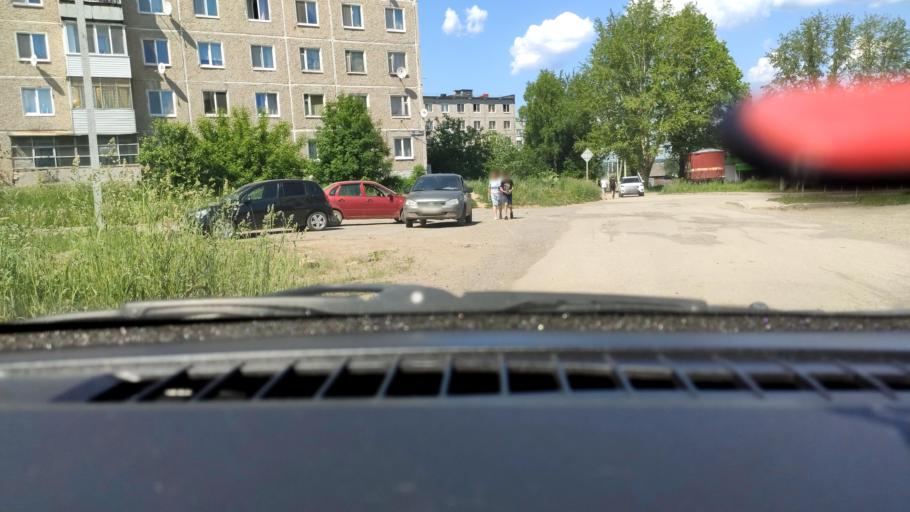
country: RU
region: Perm
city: Sylva
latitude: 58.0323
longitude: 56.7508
